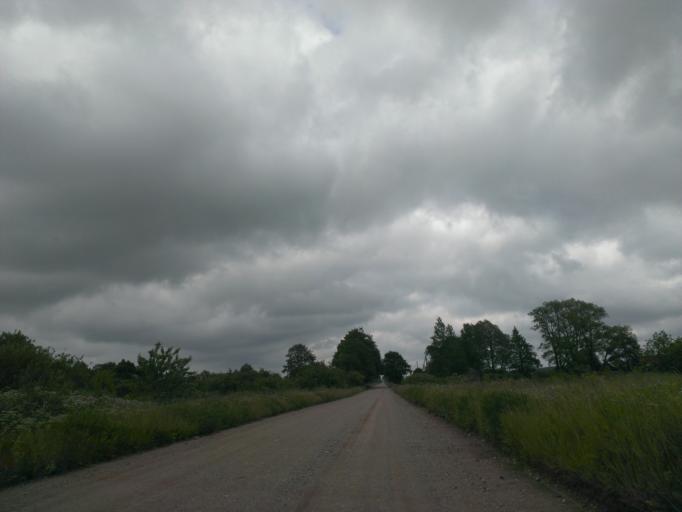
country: LV
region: Durbe
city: Liegi
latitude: 56.7509
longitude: 21.4131
